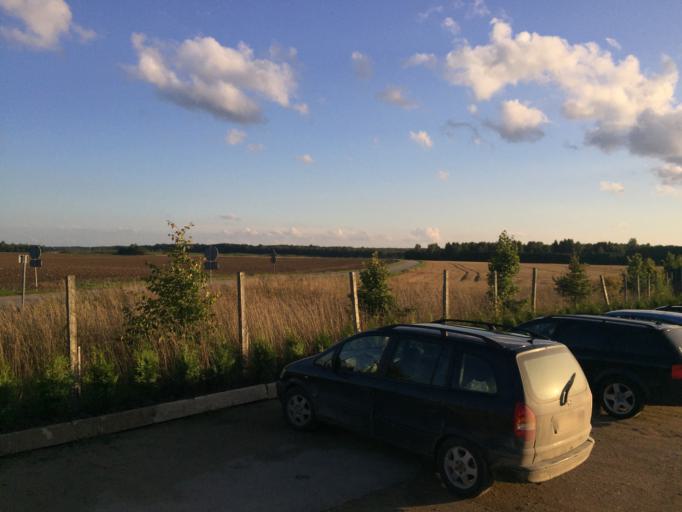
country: LV
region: Tukuma Rajons
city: Tukums
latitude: 56.8778
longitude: 23.2203
